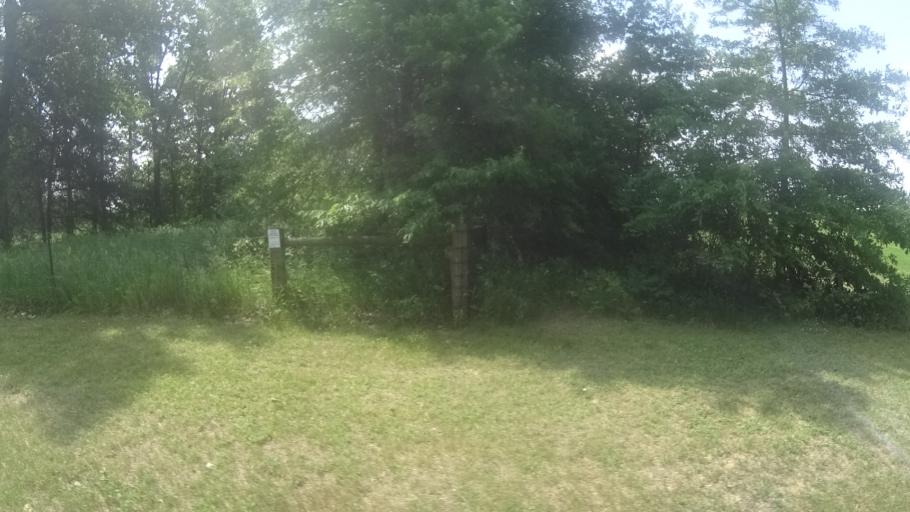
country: US
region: Ohio
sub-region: Erie County
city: Sandusky
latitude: 41.3592
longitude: -82.7128
